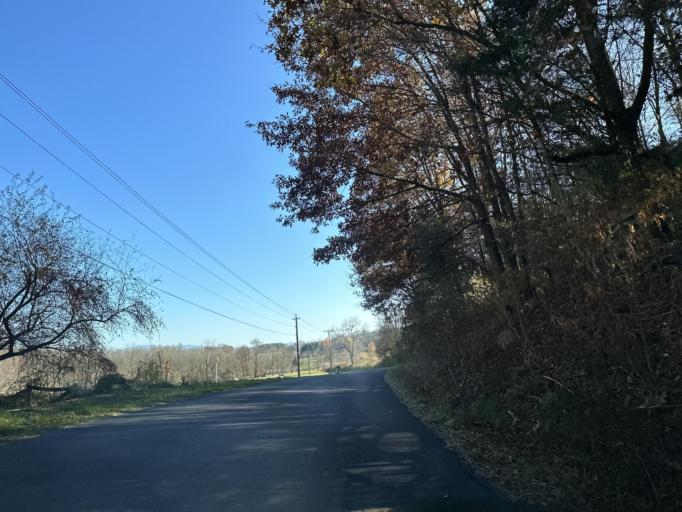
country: US
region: Virginia
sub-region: Augusta County
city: Weyers Cave
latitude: 38.3050
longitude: -78.9188
